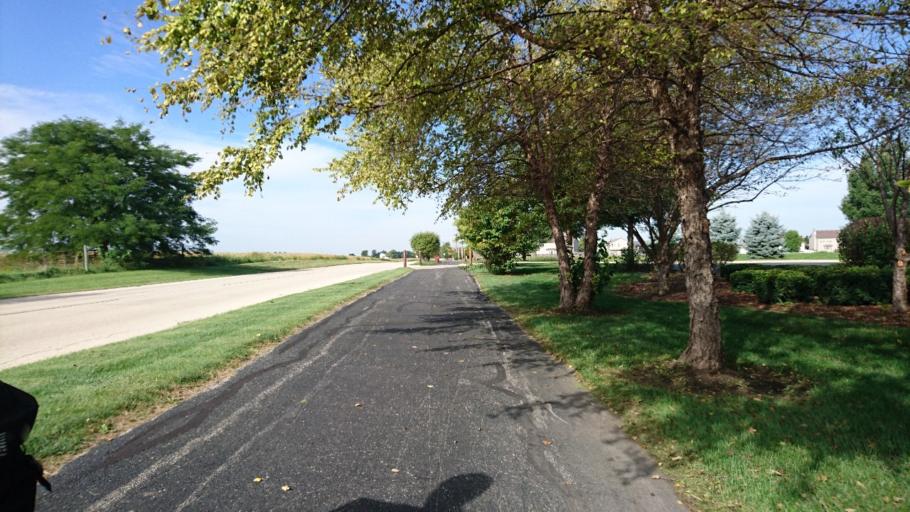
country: US
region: Illinois
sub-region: Will County
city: Manhattan
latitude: 41.4208
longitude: -88.0018
